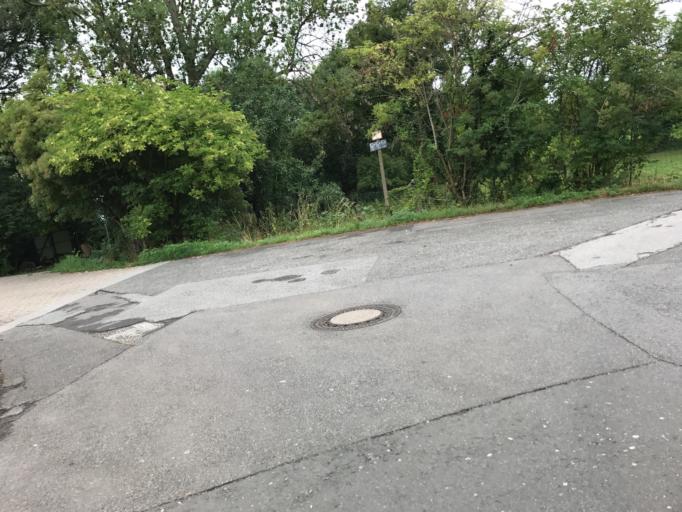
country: DE
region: North Rhine-Westphalia
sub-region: Regierungsbezirk Dusseldorf
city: Hochfeld
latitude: 51.3611
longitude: 6.6836
